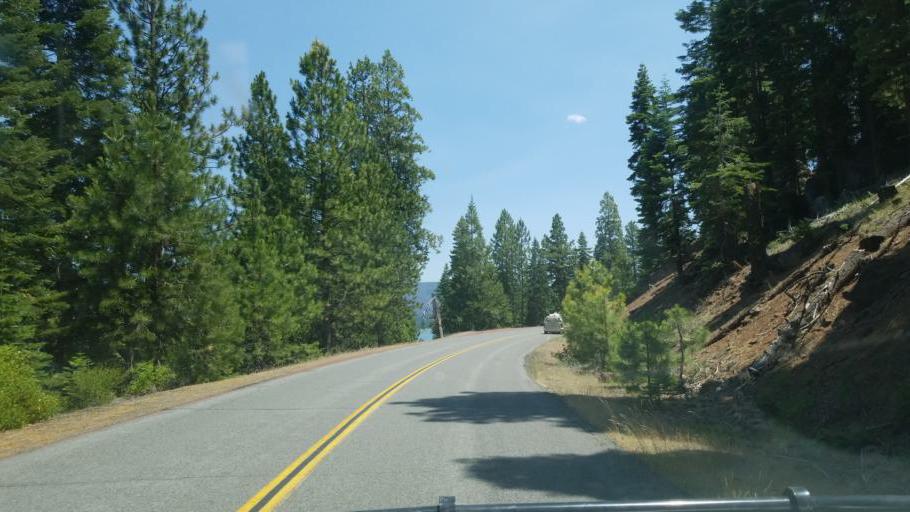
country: US
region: California
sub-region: Lassen County
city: Susanville
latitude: 40.5603
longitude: -120.8289
